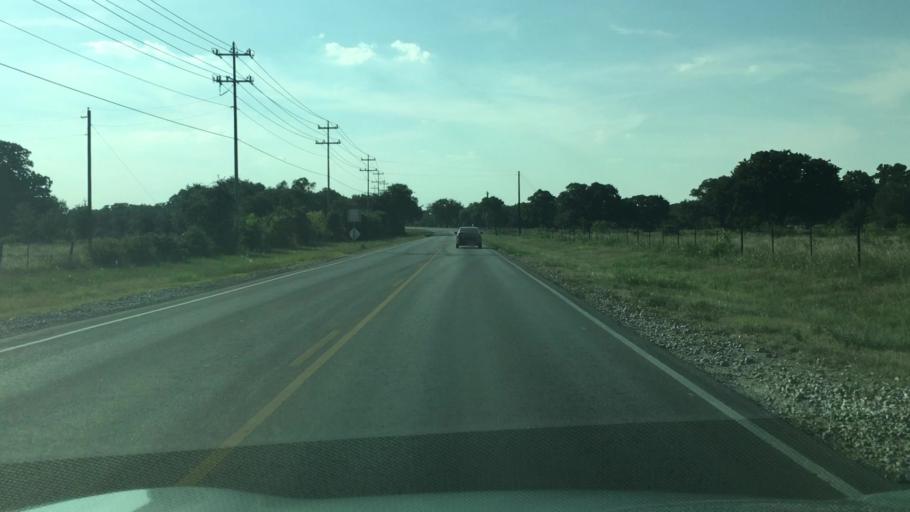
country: US
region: Texas
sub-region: Travis County
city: Shady Hollow
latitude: 30.1125
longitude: -97.9494
